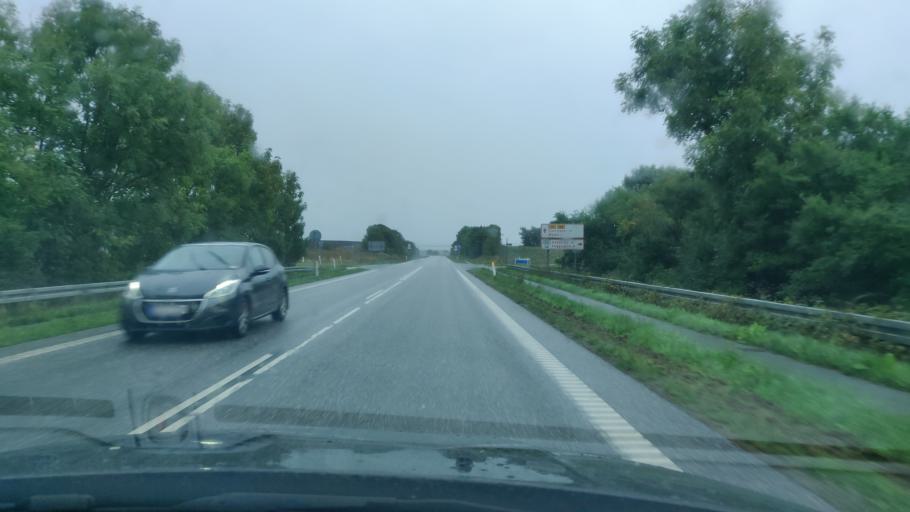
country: DK
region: North Denmark
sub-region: Vesthimmerland Kommune
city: Logstor
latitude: 57.0283
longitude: 8.9958
